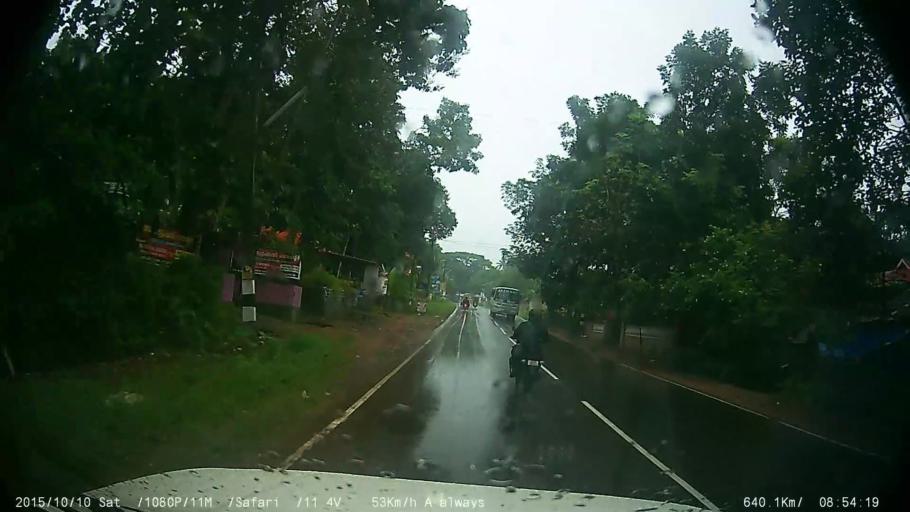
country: IN
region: Kerala
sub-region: Kottayam
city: Palackattumala
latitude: 9.7034
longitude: 76.5444
